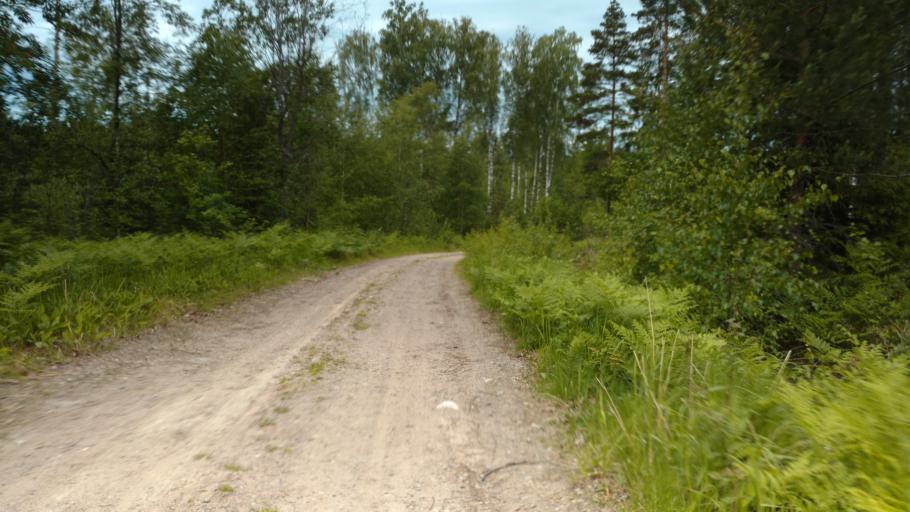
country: FI
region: Uusimaa
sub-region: Raaseporin
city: Pohja
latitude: 60.1152
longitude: 23.5498
